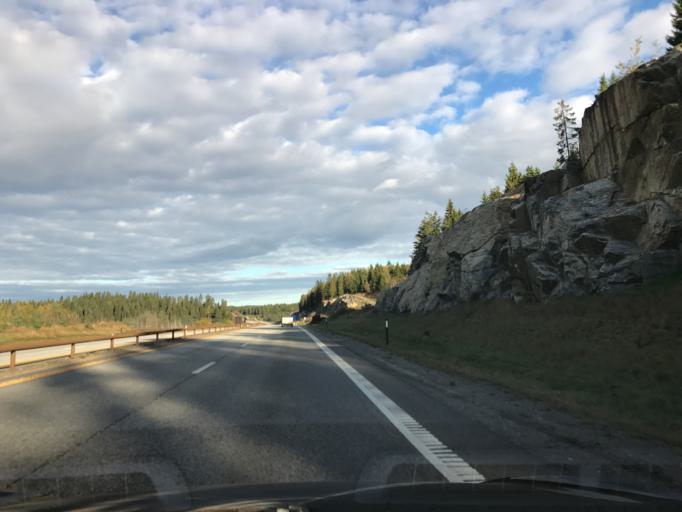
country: NO
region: Akershus
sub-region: Eidsvoll
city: Raholt
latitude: 60.2584
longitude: 11.1773
